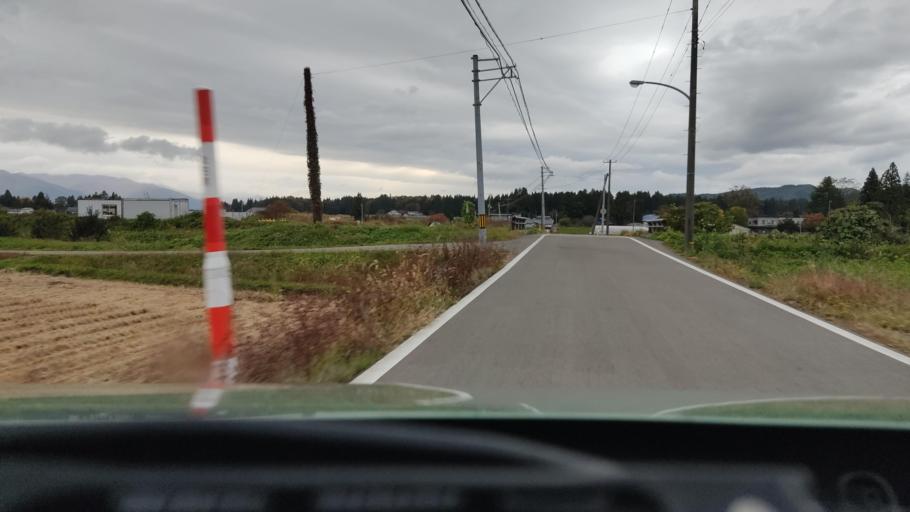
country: JP
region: Akita
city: Kakunodatemachi
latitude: 39.5654
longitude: 140.6111
